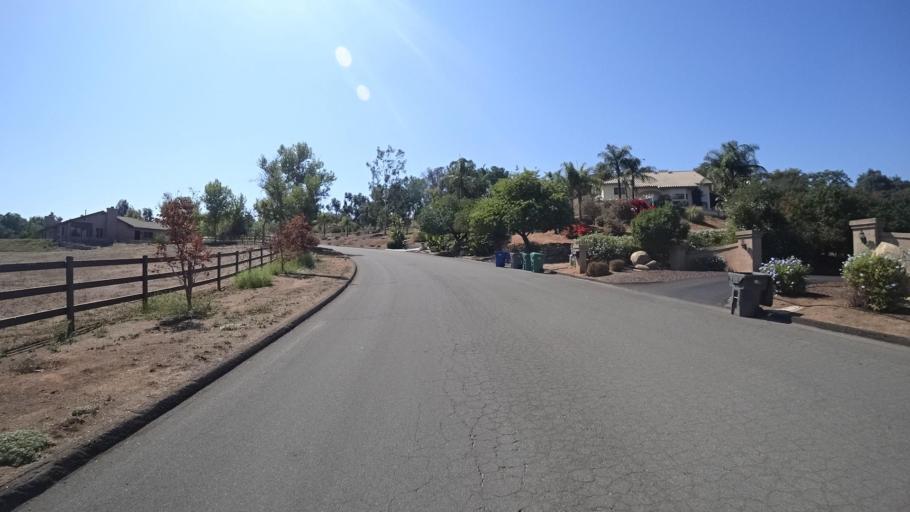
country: US
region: California
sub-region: San Diego County
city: Crest
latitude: 32.8266
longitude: -116.8566
